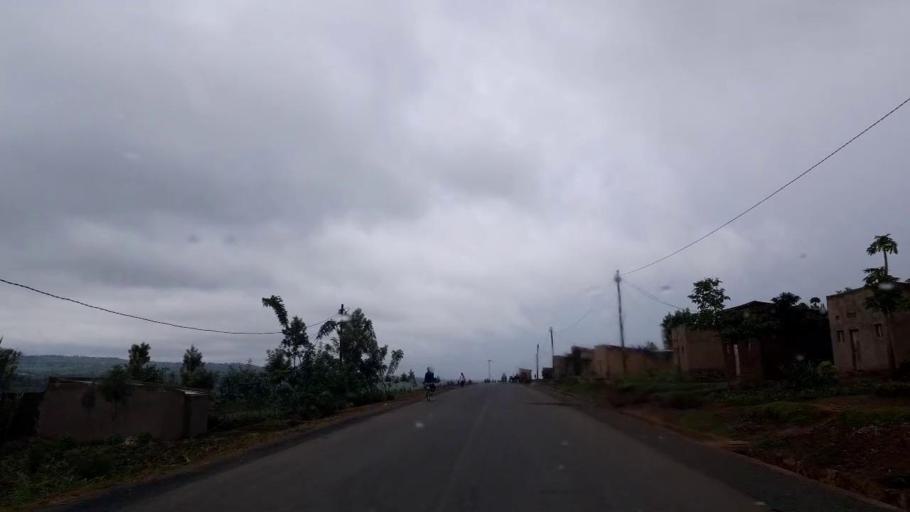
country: RW
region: Northern Province
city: Byumba
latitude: -1.4221
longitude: 30.2771
